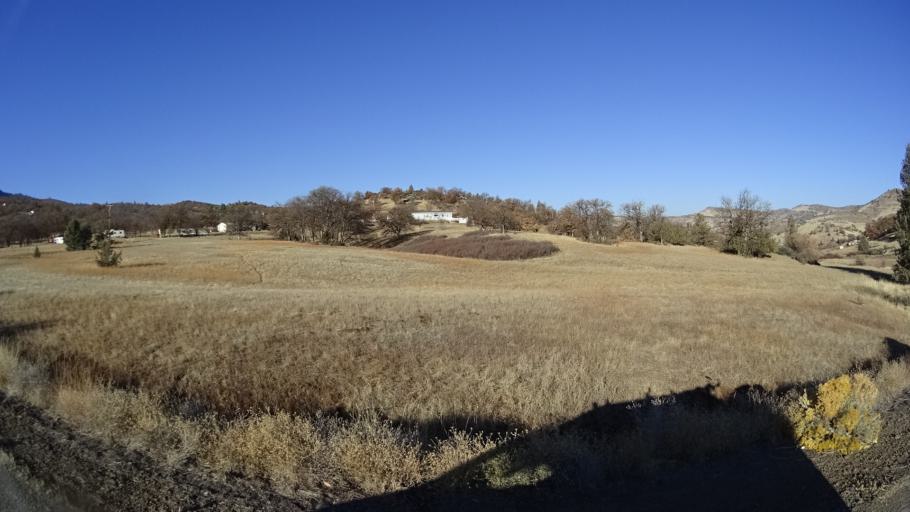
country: US
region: California
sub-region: Siskiyou County
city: Montague
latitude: 41.8905
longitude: -122.4914
